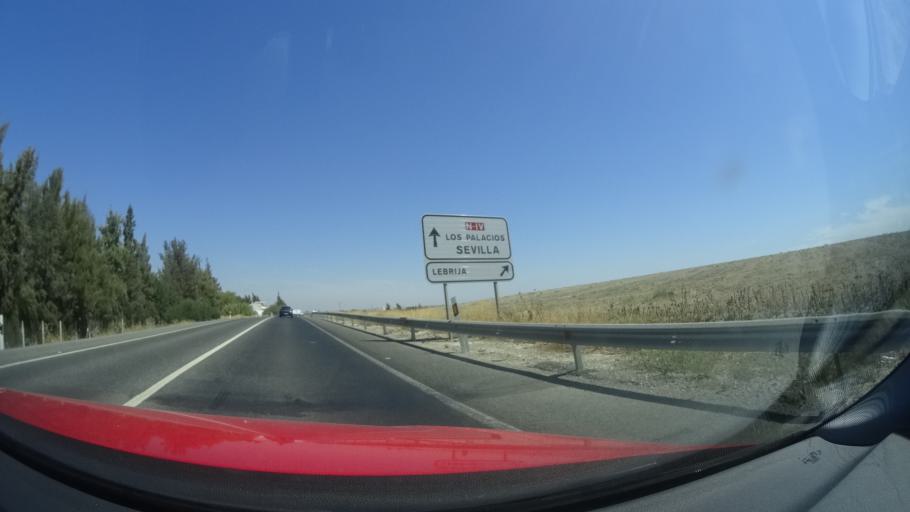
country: ES
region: Andalusia
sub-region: Provincia de Sevilla
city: Lebrija
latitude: 36.9012
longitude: -5.9873
